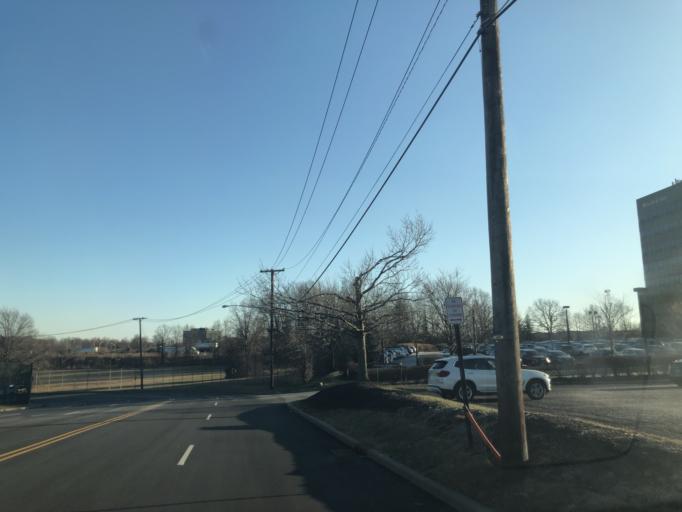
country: US
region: New Jersey
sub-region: Middlesex County
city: Woodbridge
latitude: 40.5450
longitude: -74.2996
